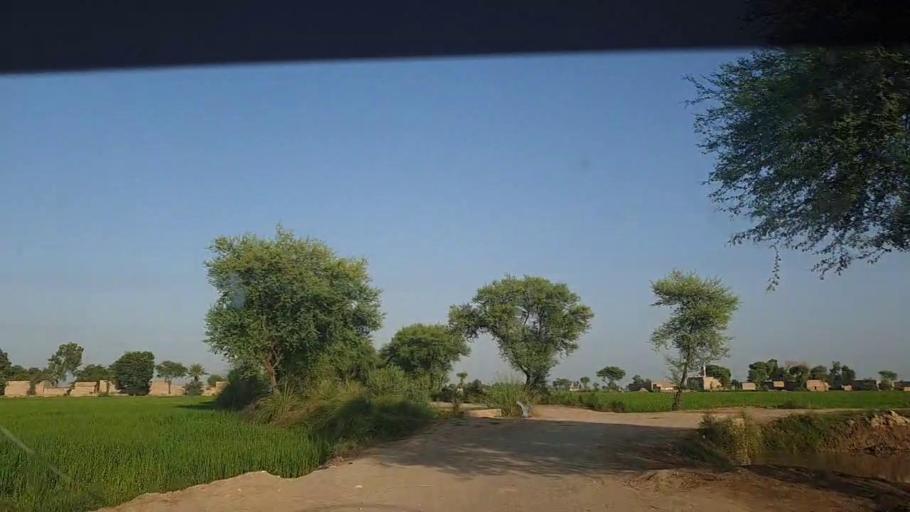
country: PK
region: Sindh
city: Thul
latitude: 28.2141
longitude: 68.8760
